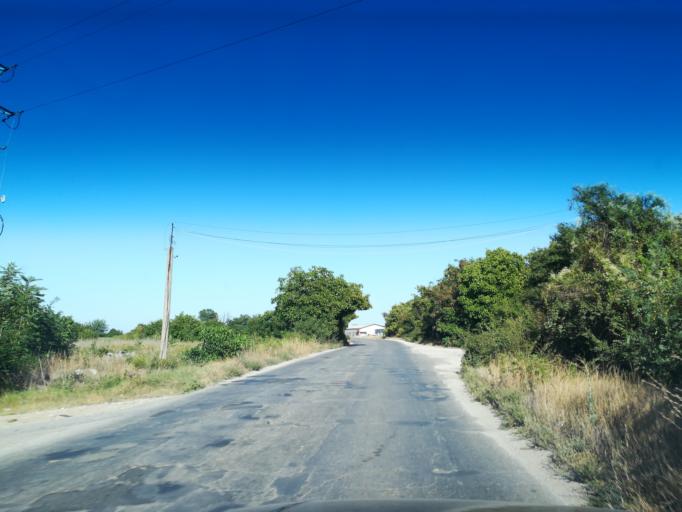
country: BG
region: Plovdiv
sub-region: Obshtina Plovdiv
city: Plovdiv
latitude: 42.1660
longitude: 24.8072
